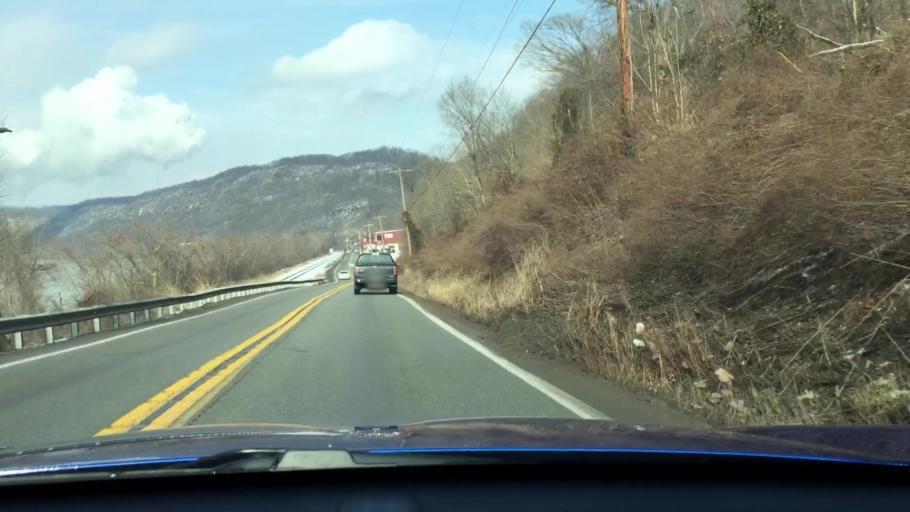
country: US
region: Pennsylvania
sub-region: Allegheny County
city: Clairton
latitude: 40.2953
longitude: -79.8649
